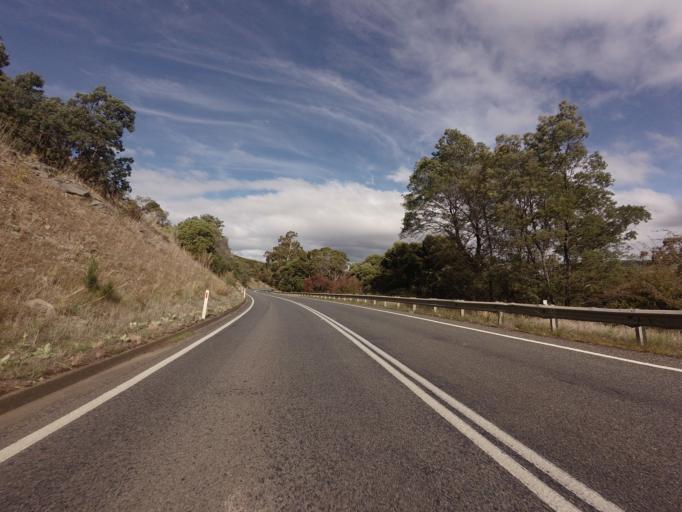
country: AU
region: Tasmania
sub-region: Derwent Valley
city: New Norfolk
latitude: -42.7263
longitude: 146.9544
